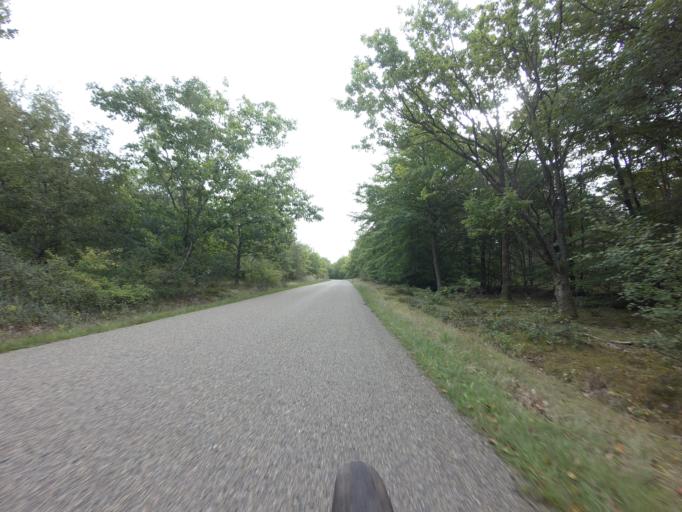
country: DK
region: North Denmark
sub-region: Hjorring Kommune
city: Hirtshals
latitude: 57.5796
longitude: 10.0474
